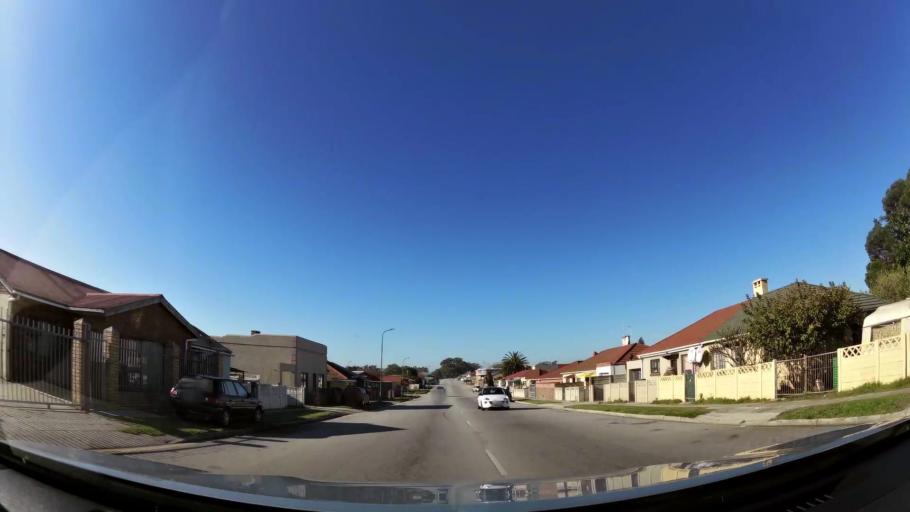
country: ZA
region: Eastern Cape
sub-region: Nelson Mandela Bay Metropolitan Municipality
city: Port Elizabeth
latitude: -33.9813
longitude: 25.6299
